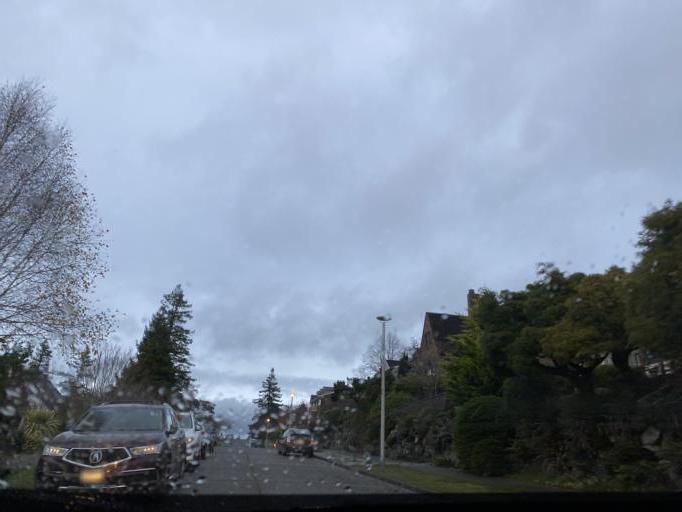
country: US
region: Washington
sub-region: King County
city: Seattle
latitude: 47.6454
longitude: -122.4119
